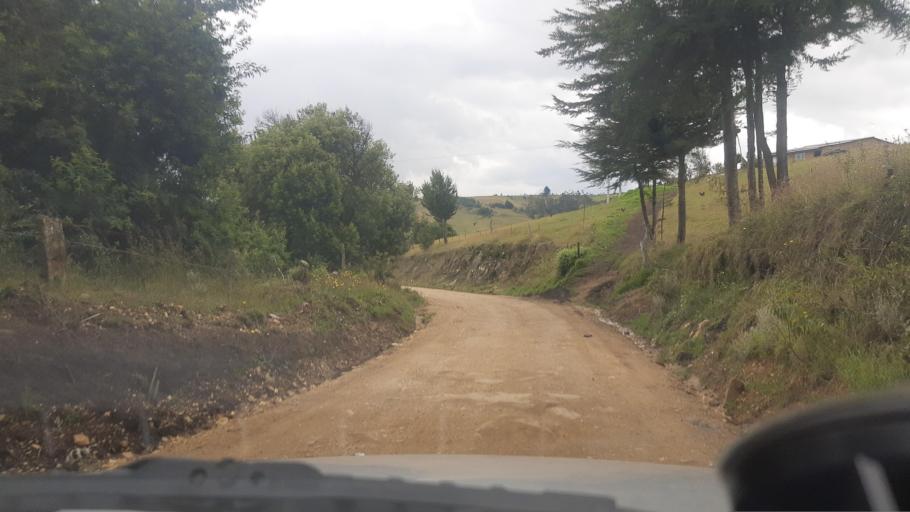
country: CO
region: Cundinamarca
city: Suesca
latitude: 5.1474
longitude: -73.7952
